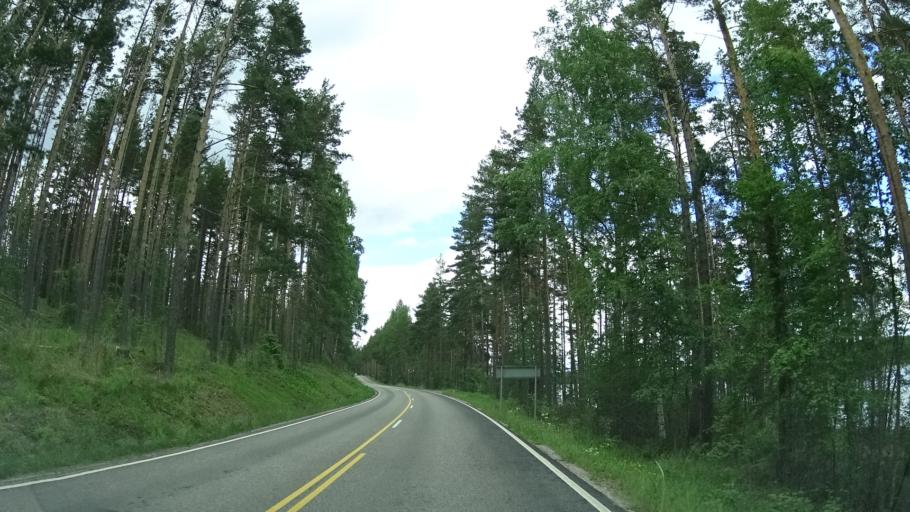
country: FI
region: Paijanne Tavastia
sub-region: Lahti
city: Asikkala
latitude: 61.3084
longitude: 25.5476
